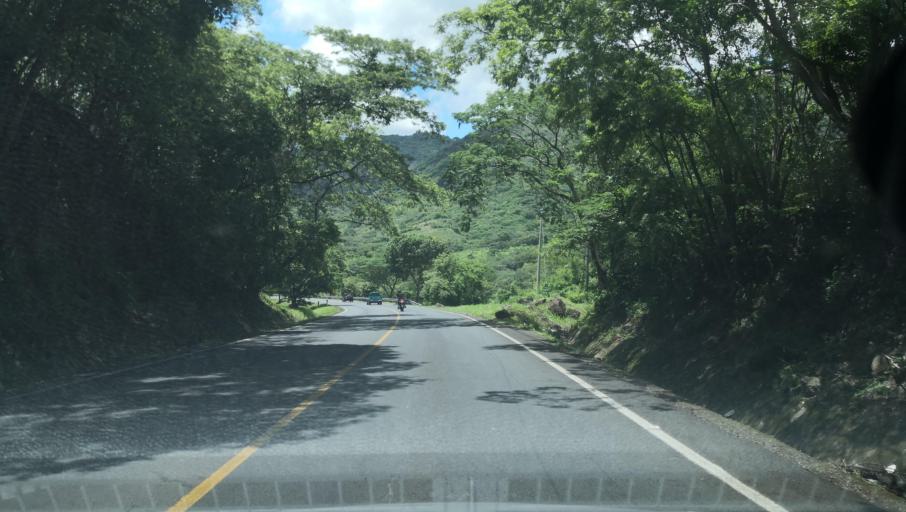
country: NI
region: Esteli
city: Condega
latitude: 13.2806
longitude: -86.3468
